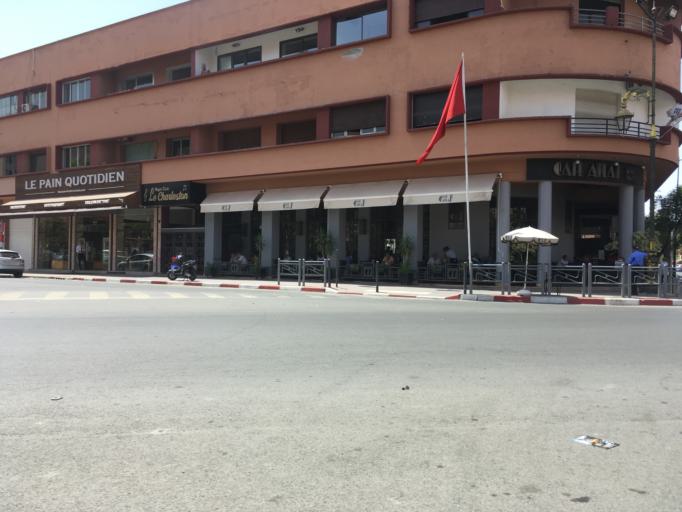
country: MA
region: Marrakech-Tensift-Al Haouz
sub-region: Marrakech
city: Marrakesh
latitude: 31.6359
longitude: -8.0143
